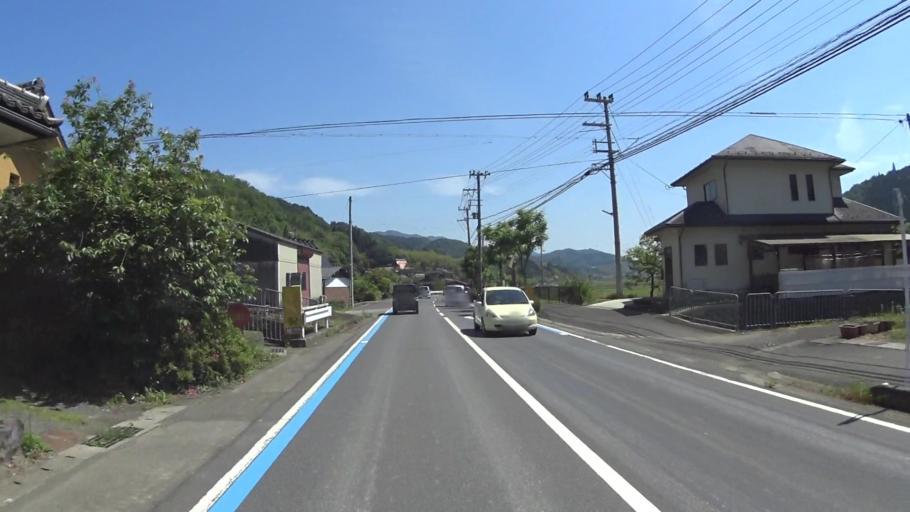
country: JP
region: Kyoto
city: Ayabe
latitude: 35.3258
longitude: 135.3313
